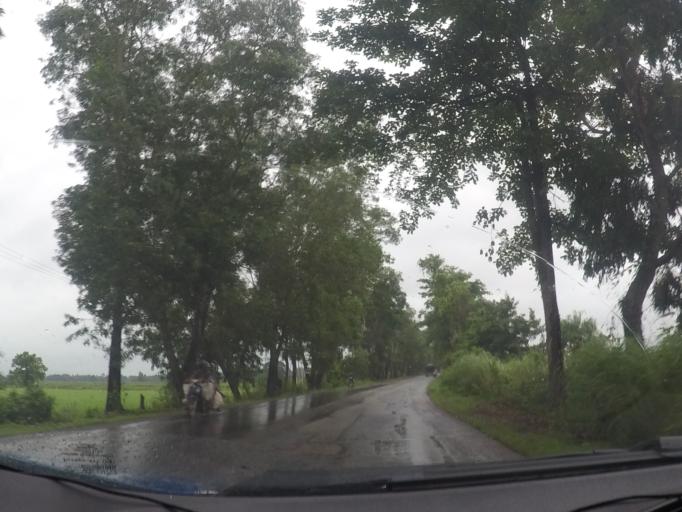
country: MM
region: Bago
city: Letpandan
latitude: 17.8991
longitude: 95.7497
